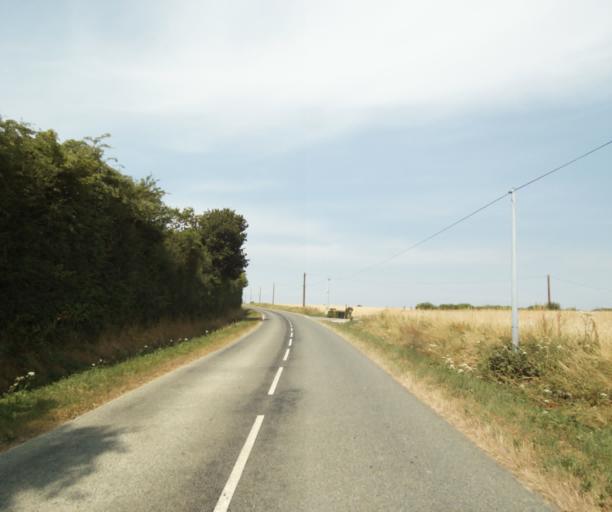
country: FR
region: Centre
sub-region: Departement d'Eure-et-Loir
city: La Bazoche-Gouet
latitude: 48.1734
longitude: 0.9841
